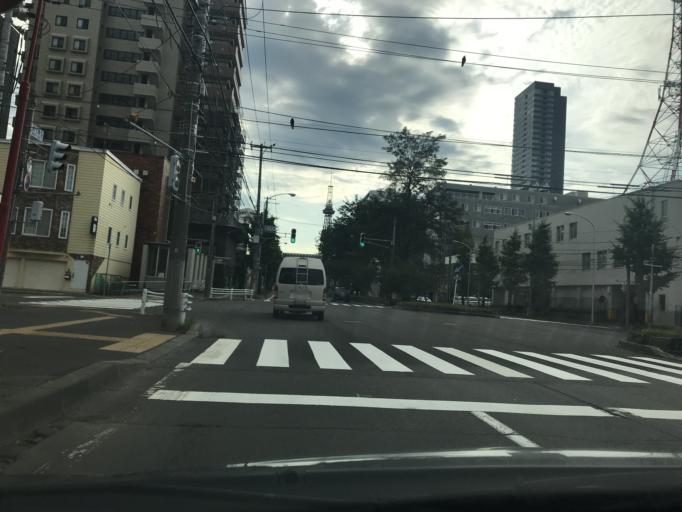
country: JP
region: Hokkaido
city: Sapporo
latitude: 43.0617
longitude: 141.3640
